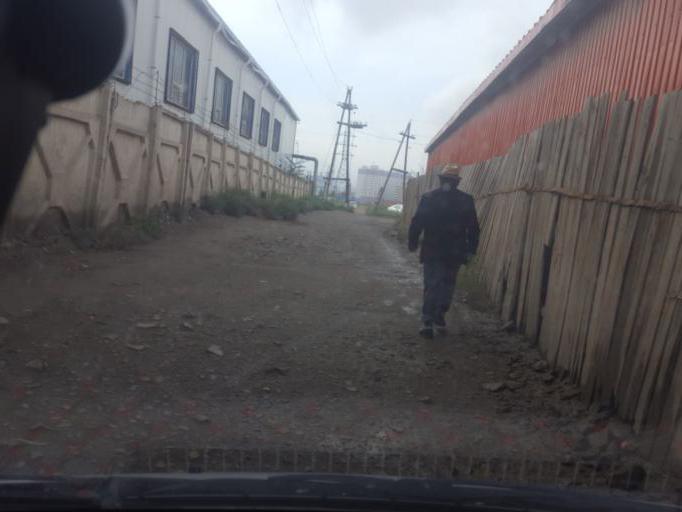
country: MN
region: Ulaanbaatar
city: Ulaanbaatar
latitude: 47.9186
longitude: 106.7995
